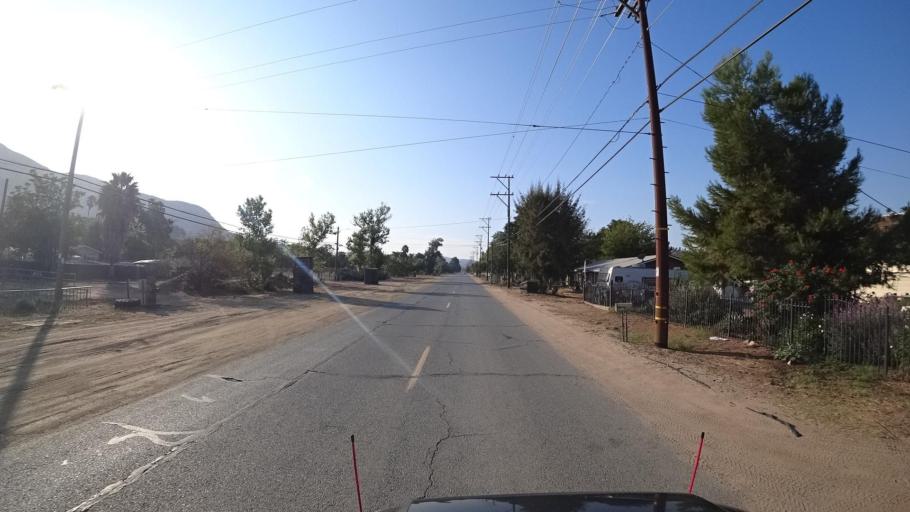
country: US
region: California
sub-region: San Diego County
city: Eucalyptus Hills
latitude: 32.8892
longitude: -116.9262
